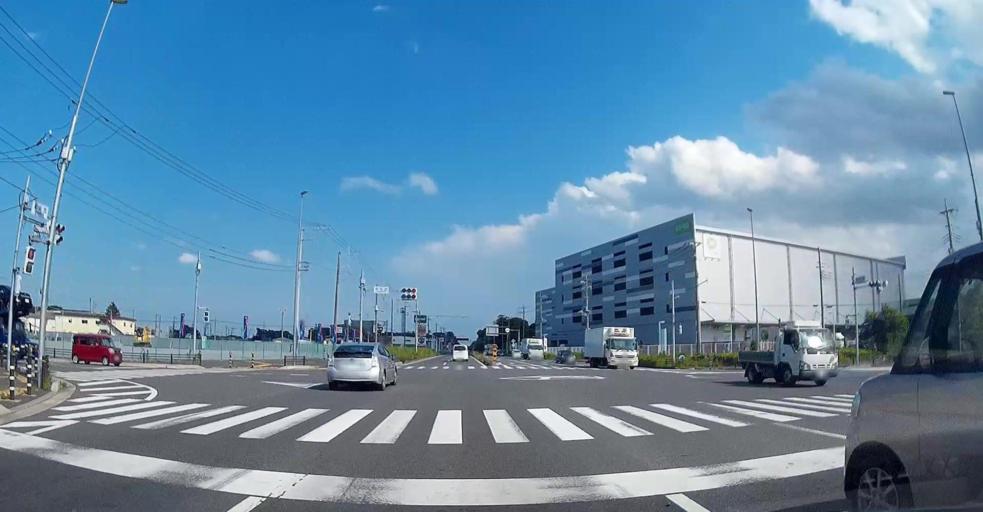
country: JP
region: Chiba
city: Noda
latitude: 35.9911
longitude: 139.8511
